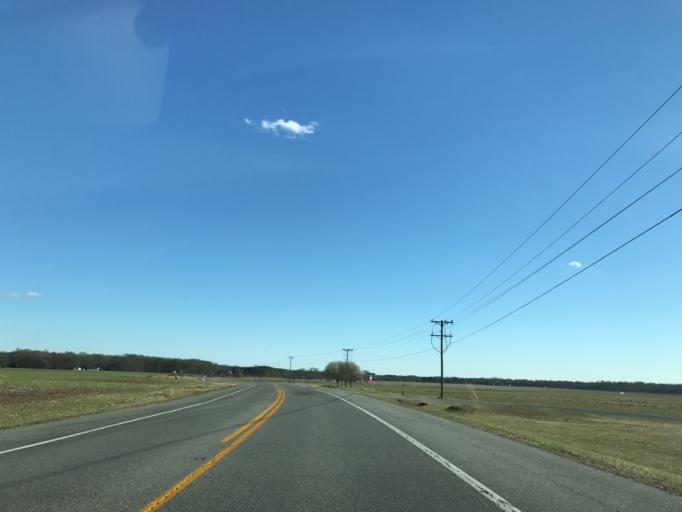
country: US
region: Maryland
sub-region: Caroline County
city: Greensboro
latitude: 39.0712
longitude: -75.8567
